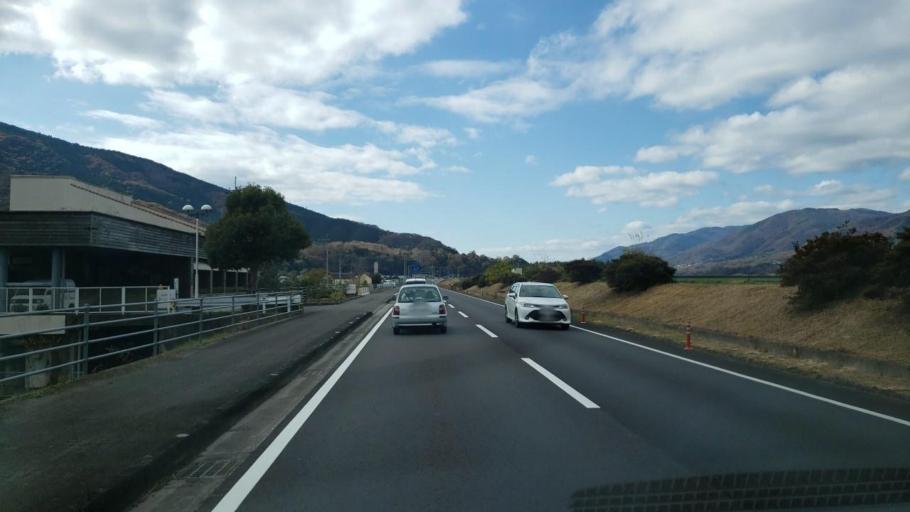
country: JP
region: Tokushima
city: Wakimachi
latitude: 34.0523
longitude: 134.1156
